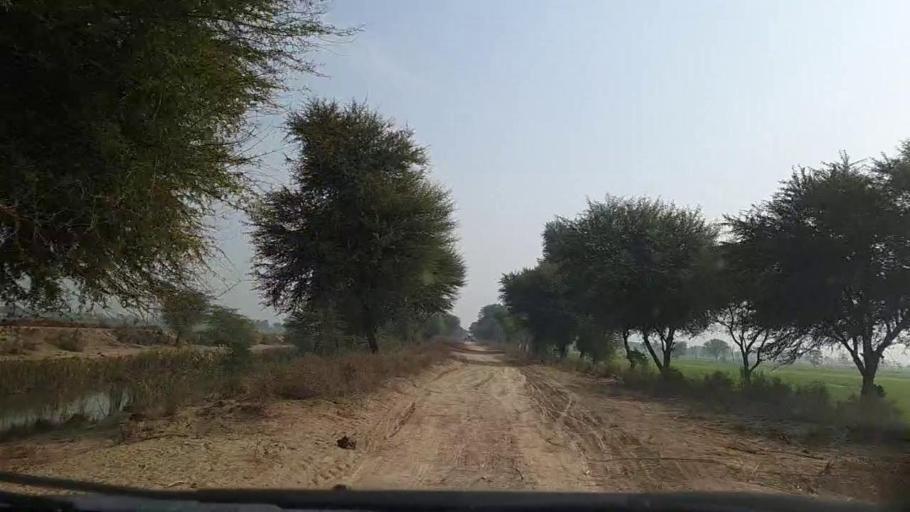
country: PK
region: Sindh
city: Sanghar
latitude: 26.0520
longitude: 68.9788
